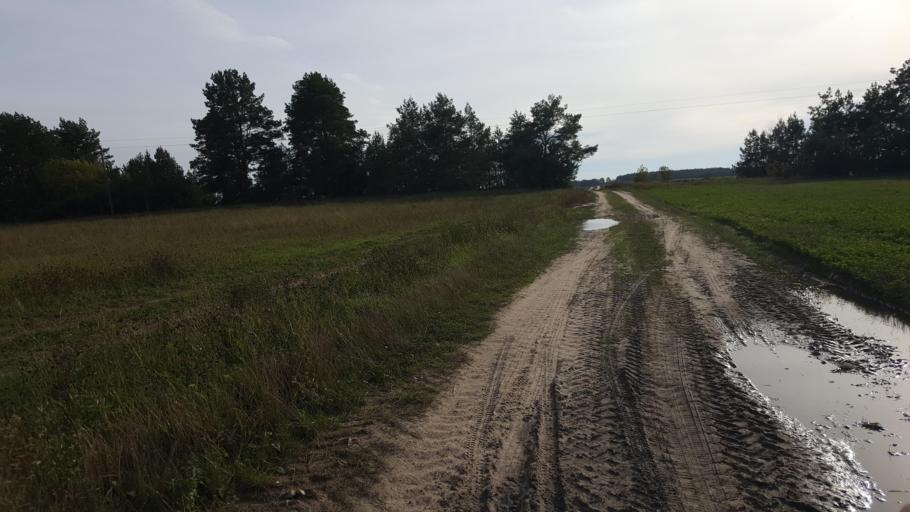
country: BY
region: Brest
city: Kamyanyets
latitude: 52.3986
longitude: 23.8555
